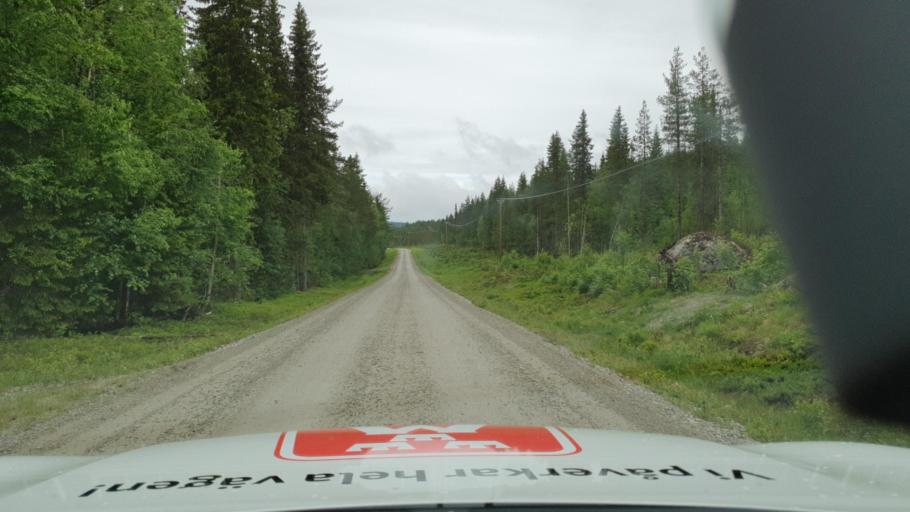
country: SE
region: Vaesterbotten
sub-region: Asele Kommun
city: Asele
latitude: 63.9668
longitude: 16.9362
